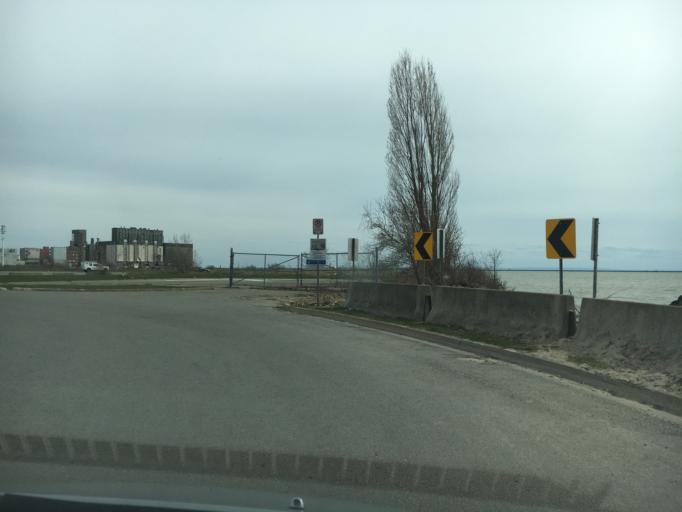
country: CA
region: Ontario
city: Port Colborne
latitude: 42.8790
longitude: -79.2600
